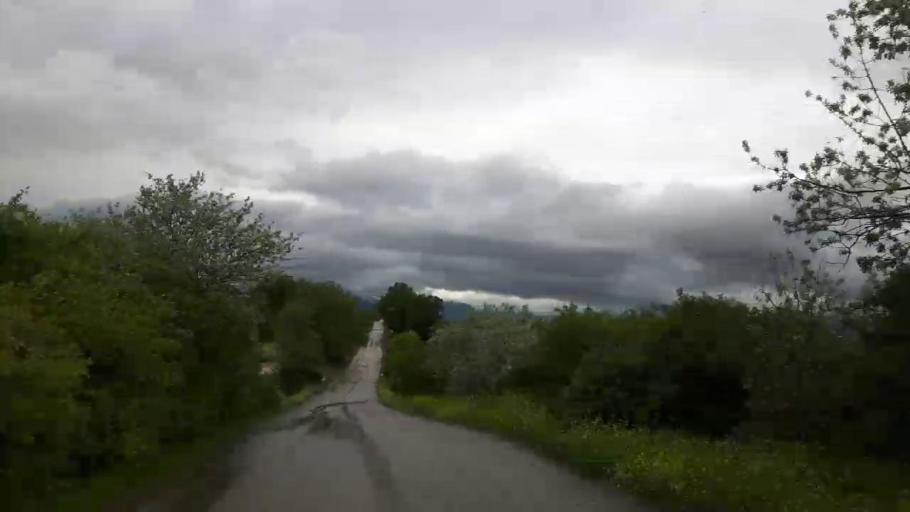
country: GE
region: Shida Kartli
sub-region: Khashuris Raioni
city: Khashuri
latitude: 41.9890
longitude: 43.7017
